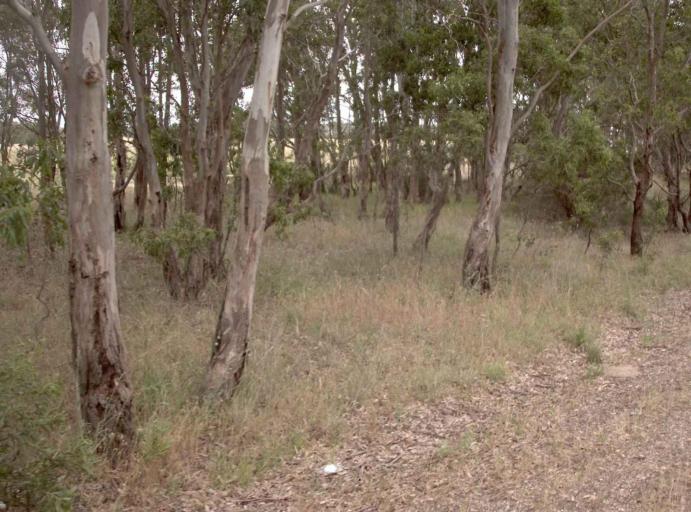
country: AU
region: Victoria
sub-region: Wellington
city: Sale
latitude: -37.9595
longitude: 147.1038
